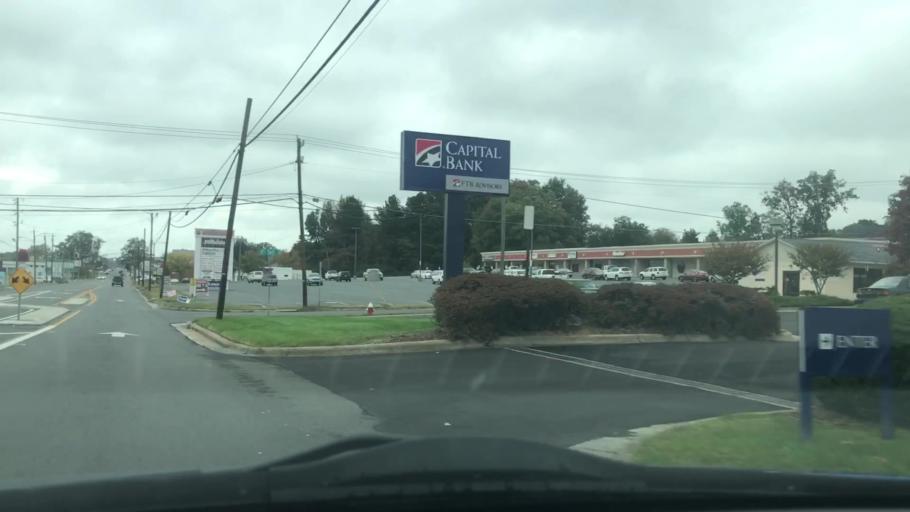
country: US
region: North Carolina
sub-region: Randolph County
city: Asheboro
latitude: 35.6919
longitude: -79.8157
